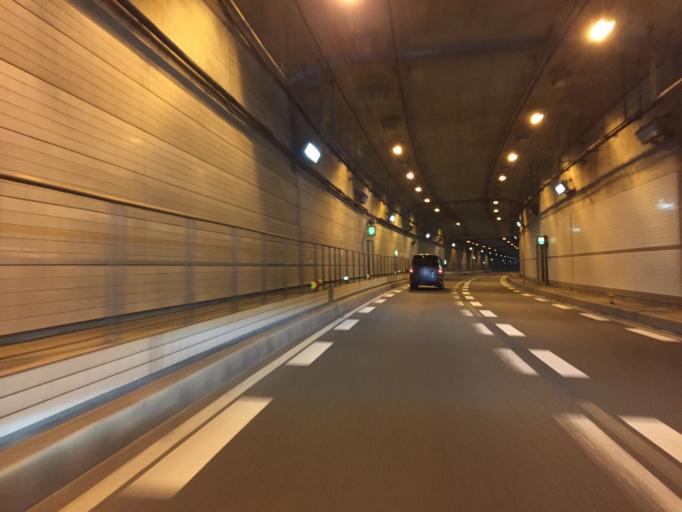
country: JP
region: Niigata
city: Niigata-shi
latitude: 37.9432
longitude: 139.0595
